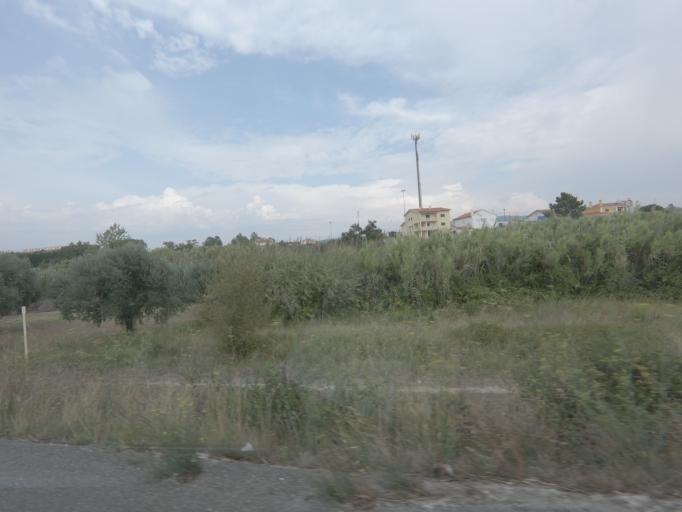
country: PT
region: Aveiro
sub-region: Mealhada
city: Pampilhosa do Botao
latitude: 40.2943
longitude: -8.4299
